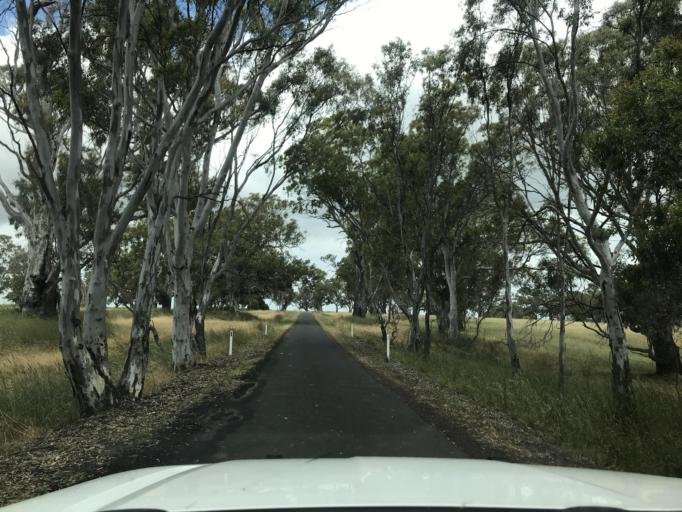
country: AU
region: South Australia
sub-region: Wattle Range
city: Penola
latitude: -37.2580
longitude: 141.5212
